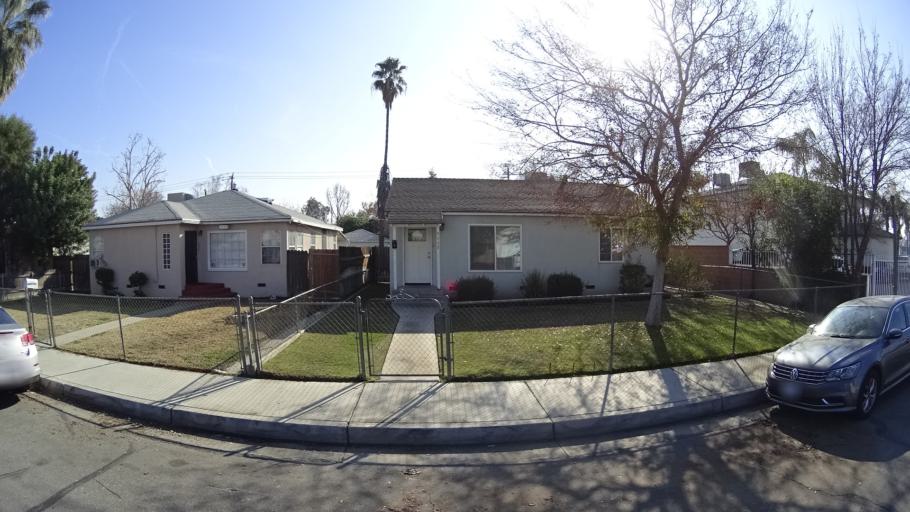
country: US
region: California
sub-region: Kern County
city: Bakersfield
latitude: 35.3667
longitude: -119.0383
